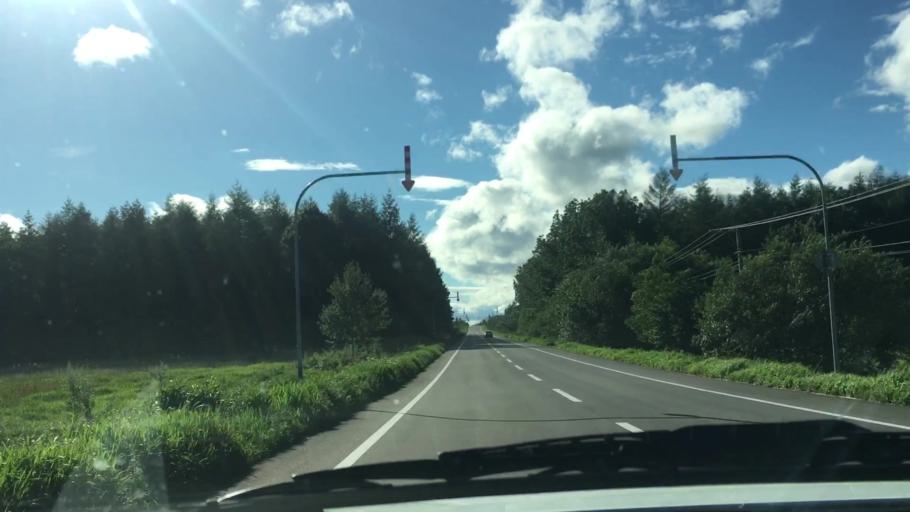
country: JP
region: Hokkaido
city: Otofuke
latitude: 43.1631
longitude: 143.1497
